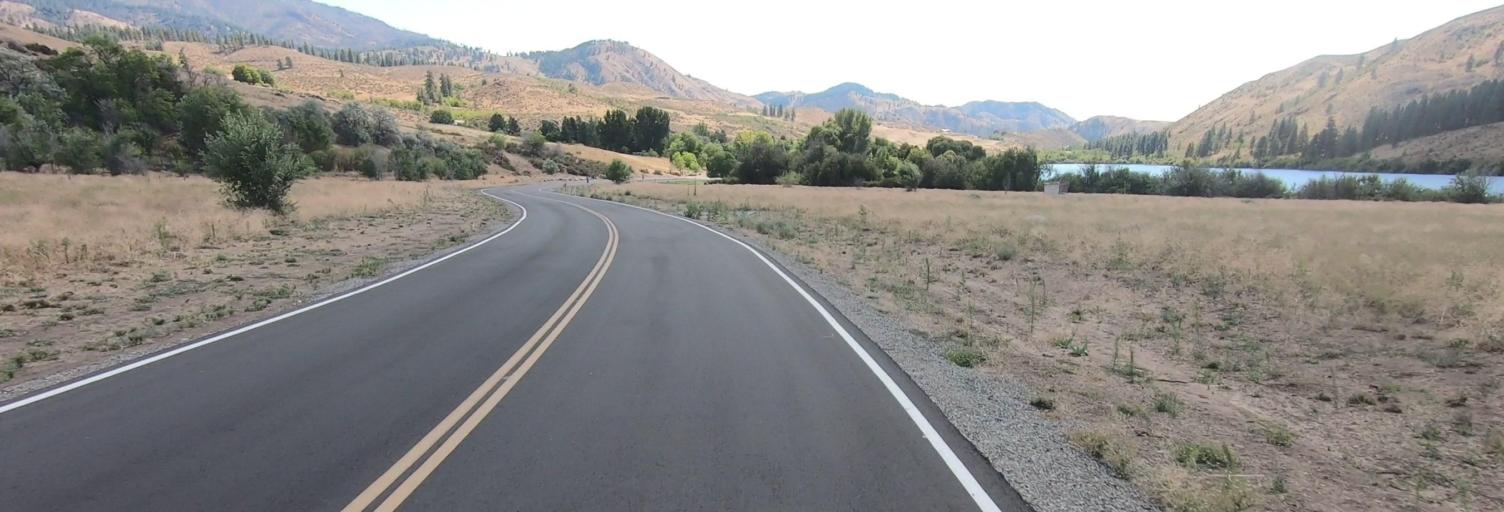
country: US
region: Washington
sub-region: Okanogan County
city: Brewster
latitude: 48.4910
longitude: -120.1517
